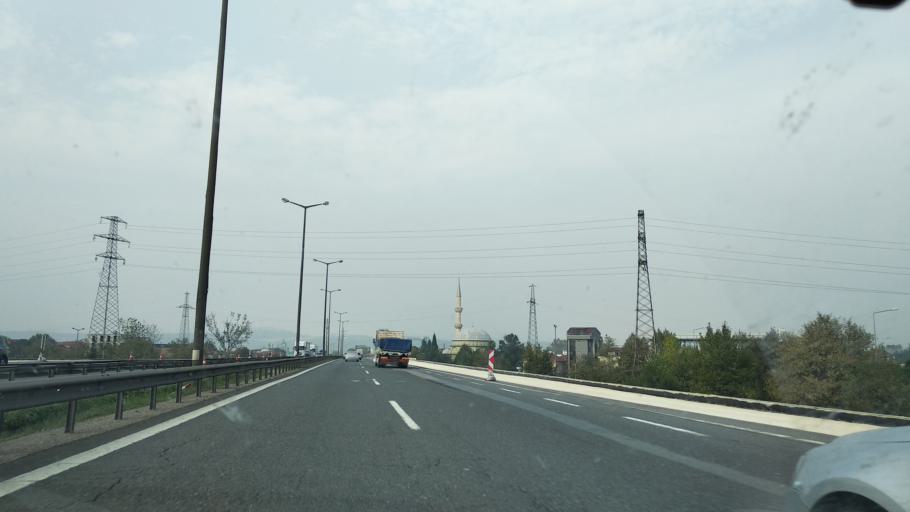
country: TR
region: Kocaeli
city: Kosekoy
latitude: 40.7493
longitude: 30.0406
